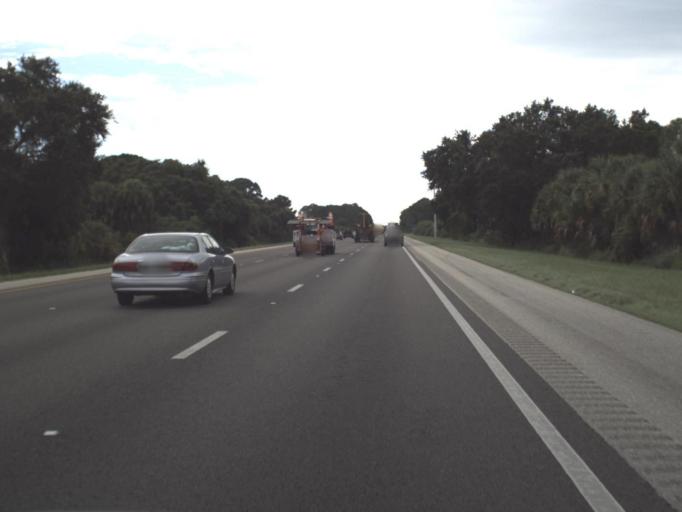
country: US
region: Florida
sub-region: Sarasota County
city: Vamo
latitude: 27.2224
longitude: -82.4501
